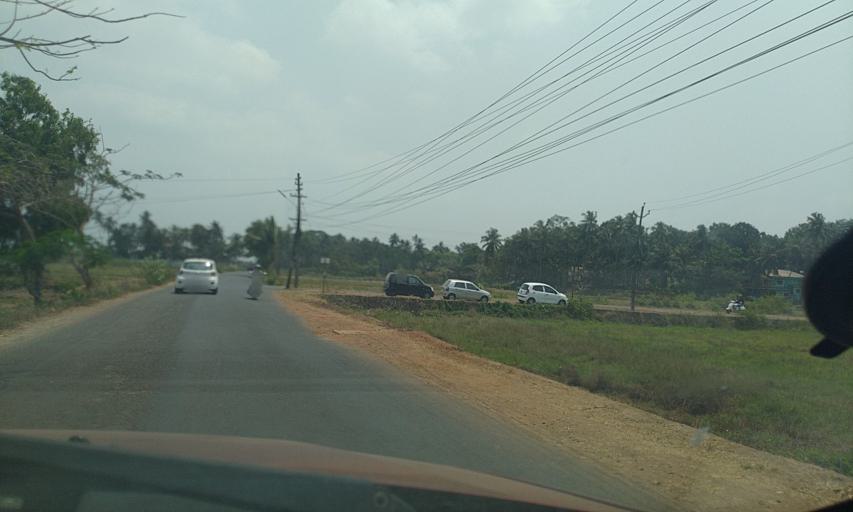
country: IN
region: Goa
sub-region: North Goa
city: Saligao
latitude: 15.5517
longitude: 73.7835
